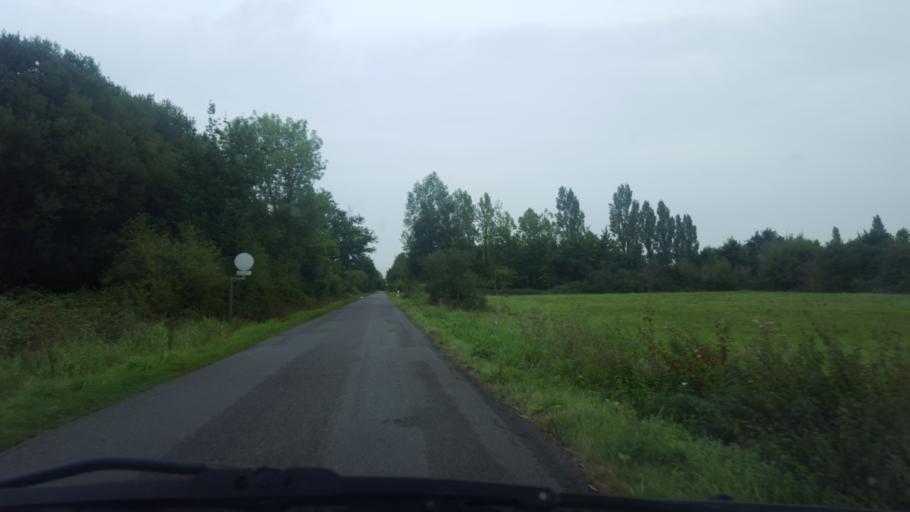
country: FR
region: Pays de la Loire
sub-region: Departement de la Loire-Atlantique
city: Saint-Philbert-de-Grand-Lieu
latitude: 47.0420
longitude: -1.6659
